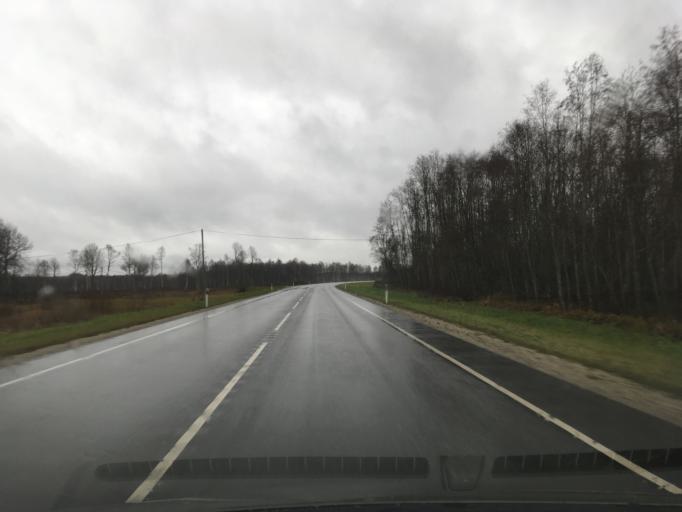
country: EE
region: Laeaene
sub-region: Lihula vald
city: Lihula
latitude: 58.7997
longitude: 24.0468
